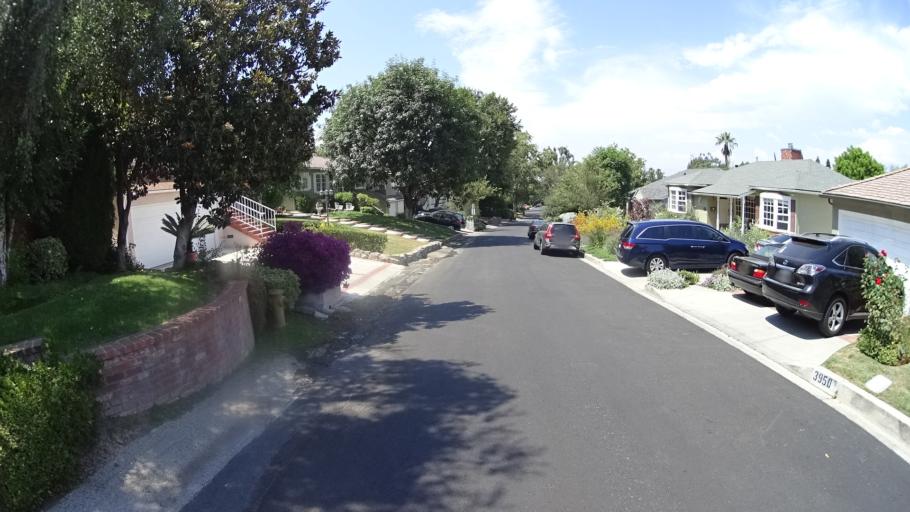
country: US
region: California
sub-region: Los Angeles County
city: Sherman Oaks
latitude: 34.1418
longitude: -118.4147
